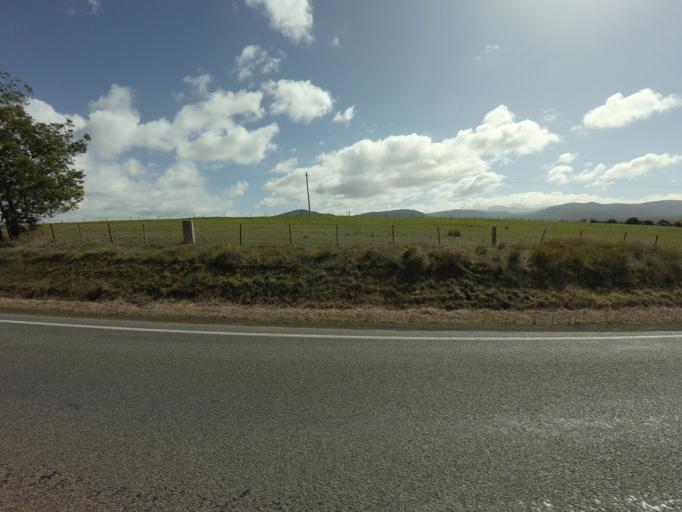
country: AU
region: Tasmania
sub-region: Northern Midlands
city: Evandale
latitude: -41.7990
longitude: 147.7014
